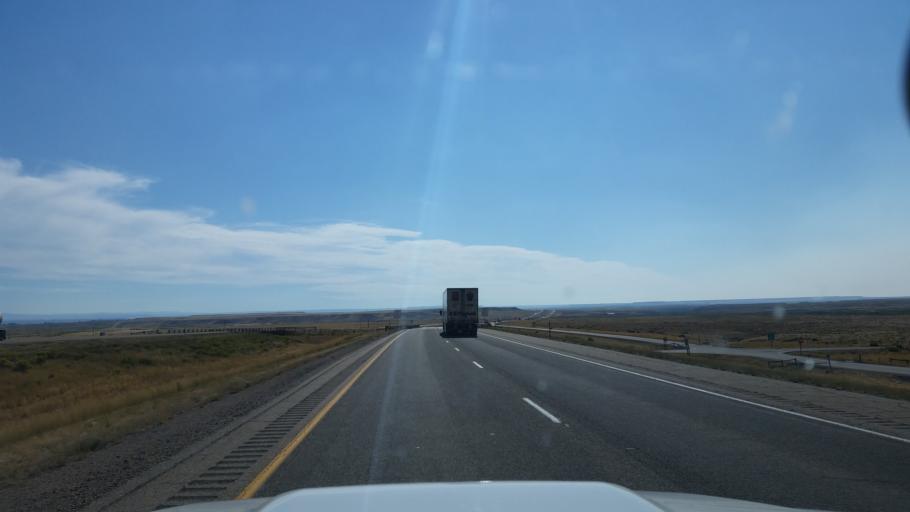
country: US
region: Wyoming
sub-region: Uinta County
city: Lyman
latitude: 41.3936
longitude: -110.1829
